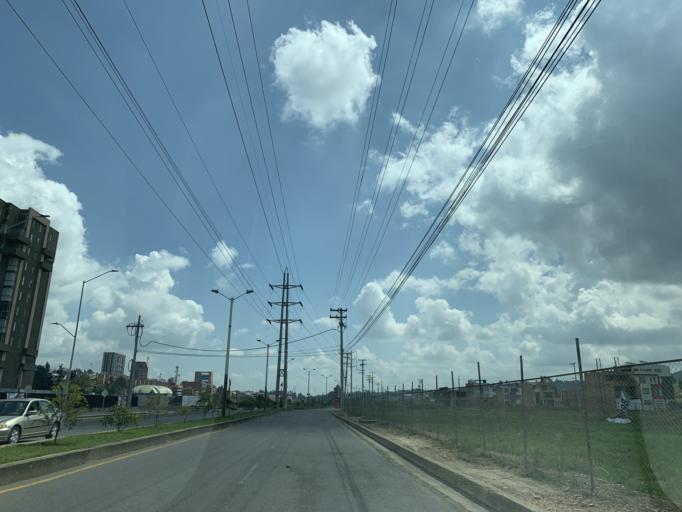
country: CO
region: Boyaca
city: Tunja
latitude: 5.5606
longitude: -73.3422
